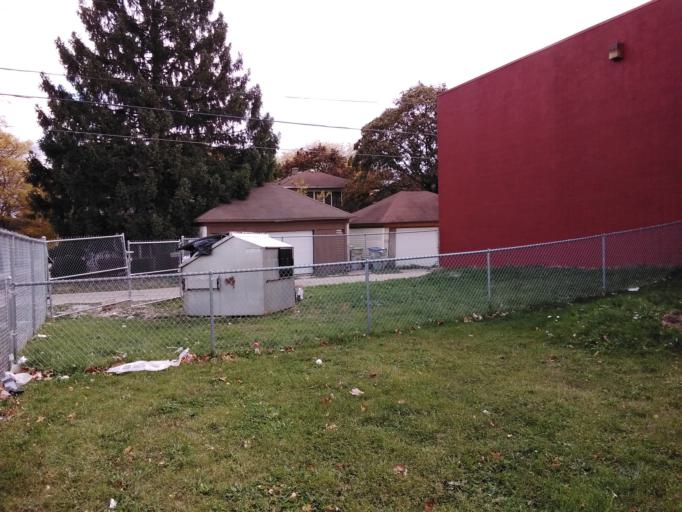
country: US
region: Wisconsin
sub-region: Milwaukee County
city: Glendale
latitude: 43.1137
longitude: -87.9560
